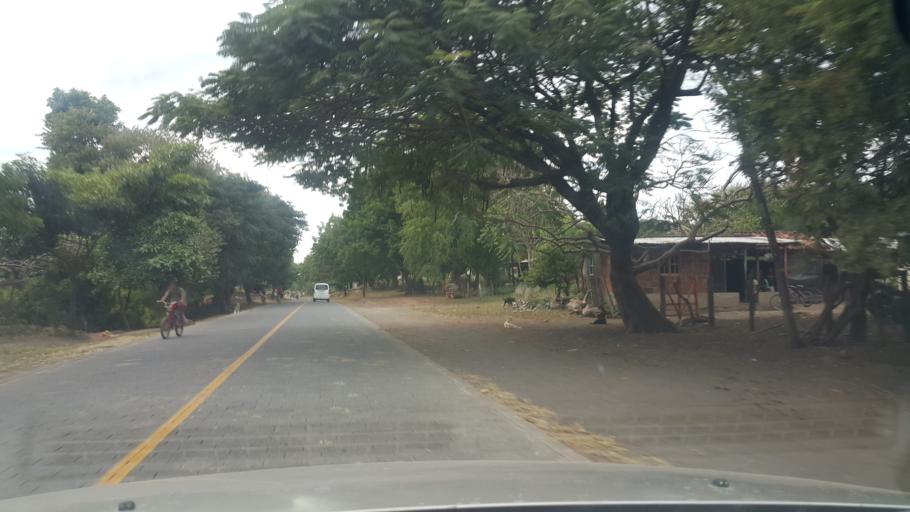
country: NI
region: Rivas
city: Moyogalpa
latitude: 11.4957
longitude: -85.6891
